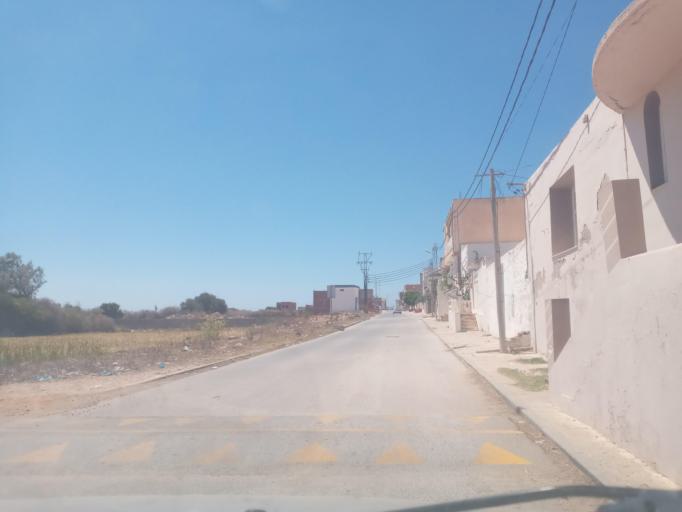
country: TN
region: Nabul
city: El Haouaria
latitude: 37.0489
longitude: 11.0055
